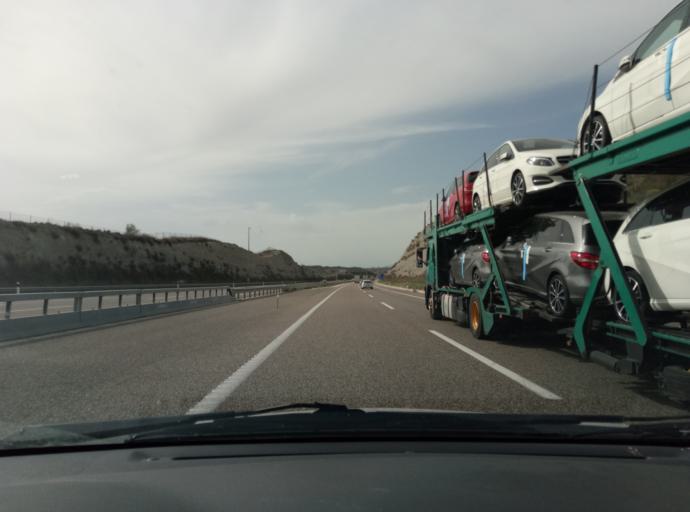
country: ES
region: Catalonia
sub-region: Provincia de Lleida
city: Cervera
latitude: 41.6384
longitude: 1.3331
